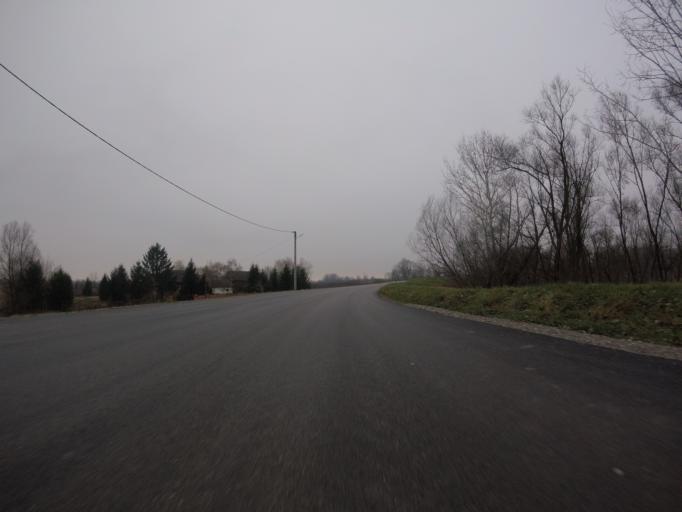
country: HR
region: Sisacko-Moslavacka
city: Lekenik
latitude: 45.6666
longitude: 16.2481
